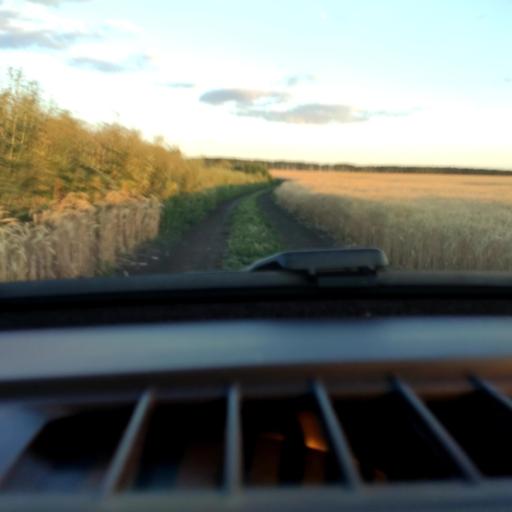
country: RU
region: Voronezj
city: Verkhnyaya Khava
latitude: 51.5870
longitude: 39.8708
